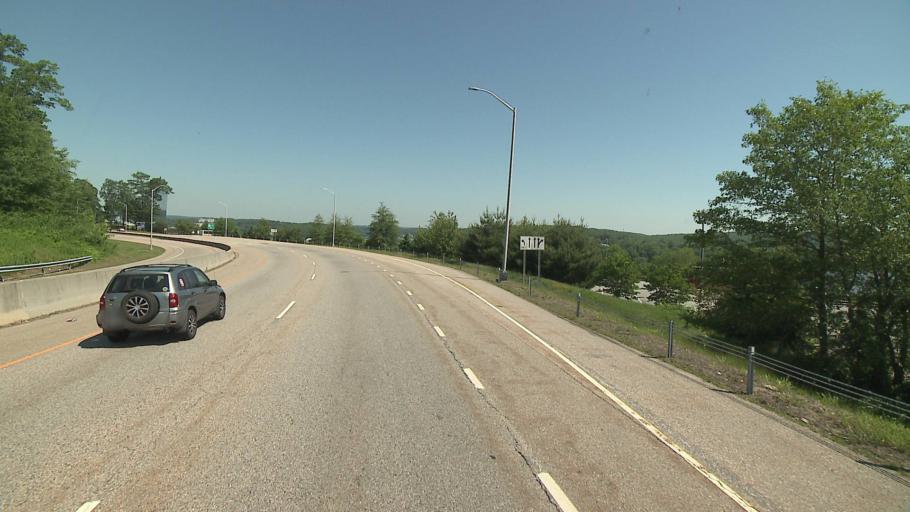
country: US
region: Connecticut
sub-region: New London County
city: Norwich
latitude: 41.4821
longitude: -72.0787
